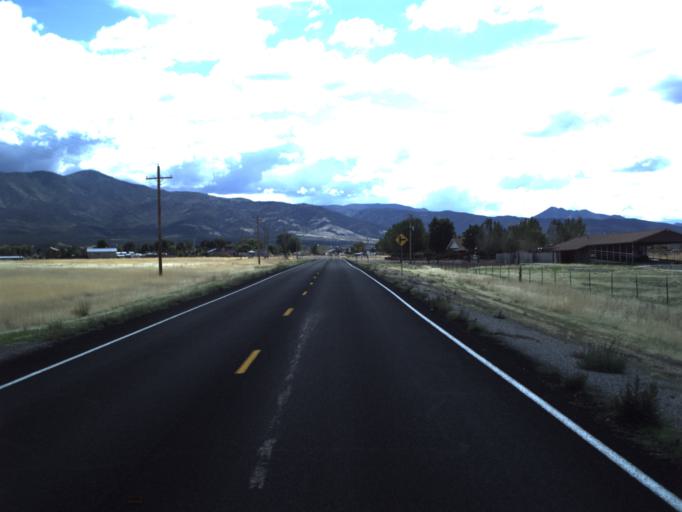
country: US
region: Utah
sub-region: Millard County
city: Fillmore
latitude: 38.8135
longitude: -112.4363
